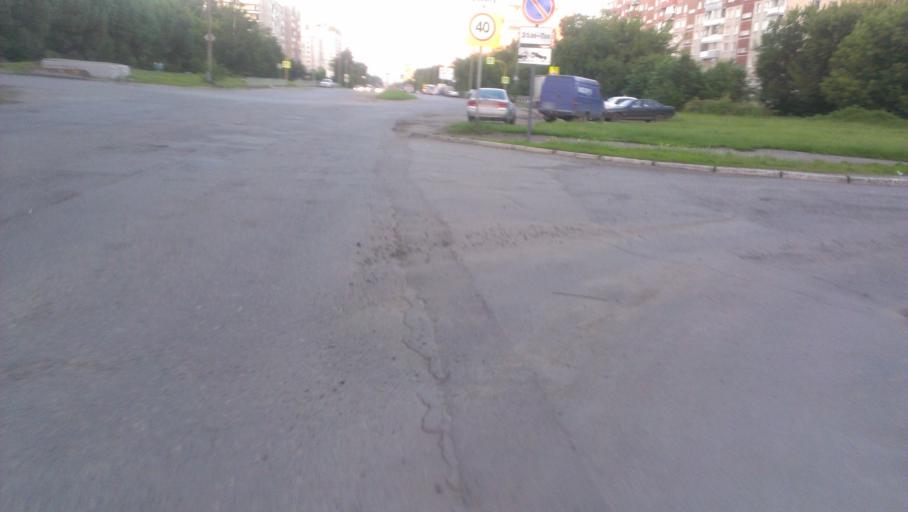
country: RU
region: Altai Krai
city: Novosilikatnyy
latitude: 53.3628
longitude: 83.6667
